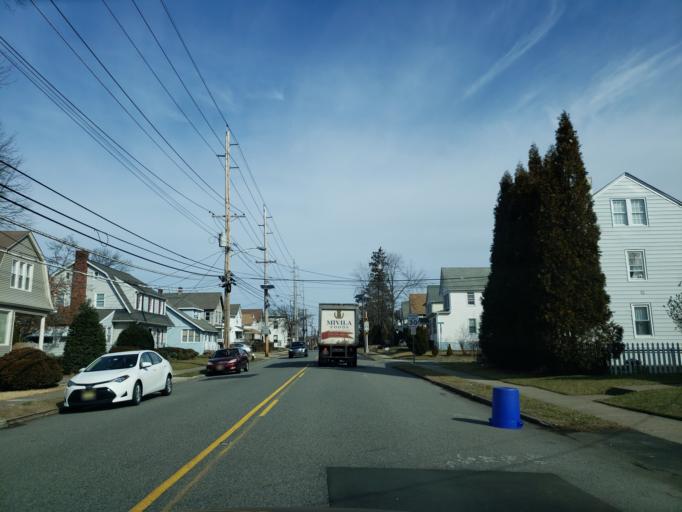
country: US
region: New Jersey
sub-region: Passaic County
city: Singac
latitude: 40.8783
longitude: -74.2301
